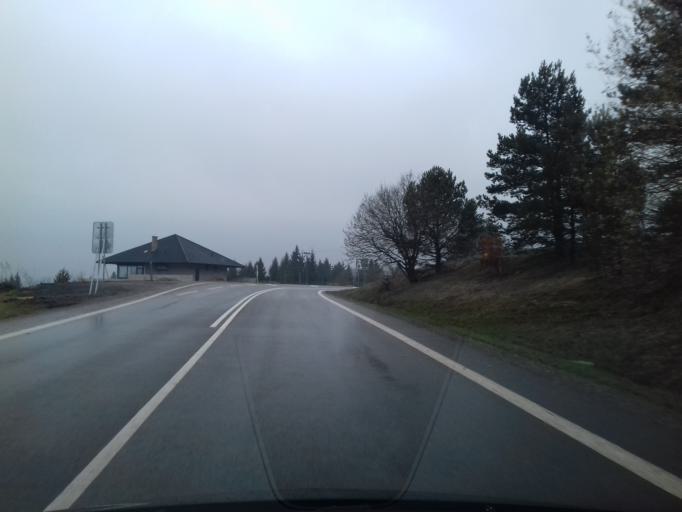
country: SK
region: Presovsky
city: Stara L'ubovna
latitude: 49.3453
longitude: 20.6750
